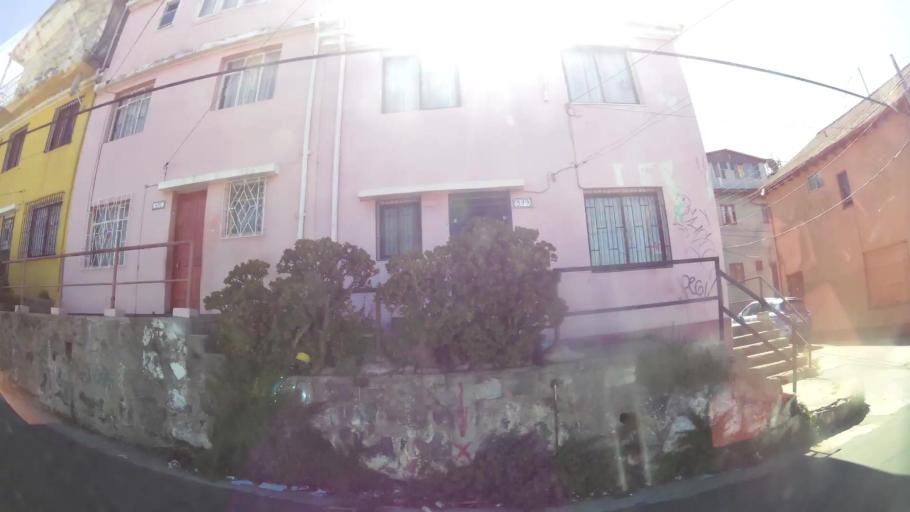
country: CL
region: Valparaiso
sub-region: Provincia de Valparaiso
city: Valparaiso
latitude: -33.0247
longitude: -71.6336
